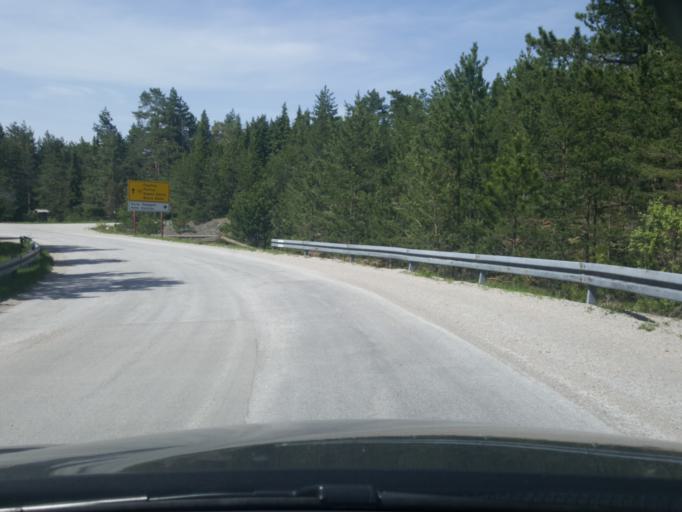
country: RS
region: Central Serbia
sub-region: Zlatiborski Okrug
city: Bajina Basta
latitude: 43.8857
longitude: 19.5433
